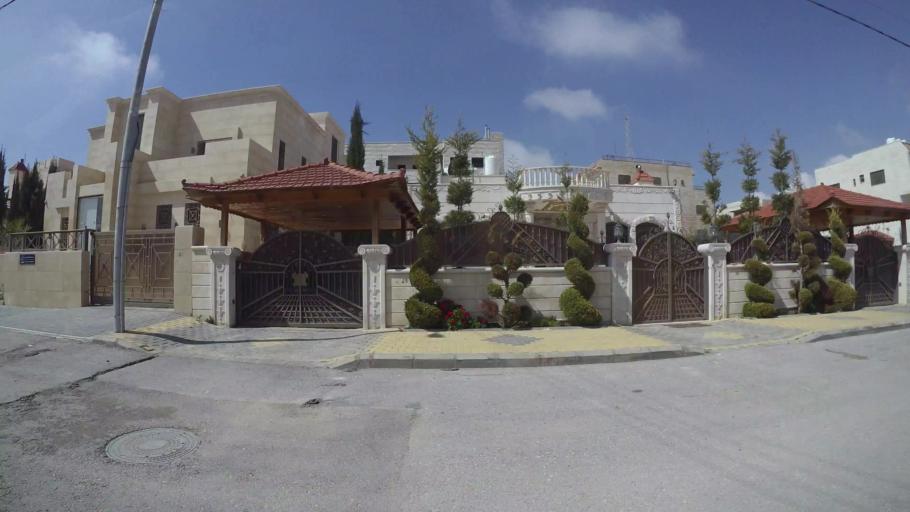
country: JO
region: Amman
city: Al Bunayyat ash Shamaliyah
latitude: 31.8987
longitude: 35.8893
